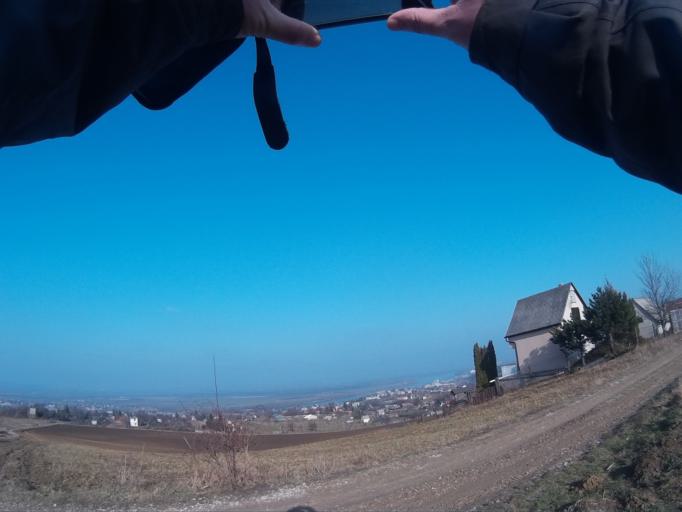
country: HU
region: Komarom-Esztergom
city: Labatlan
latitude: 47.7392
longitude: 18.4821
